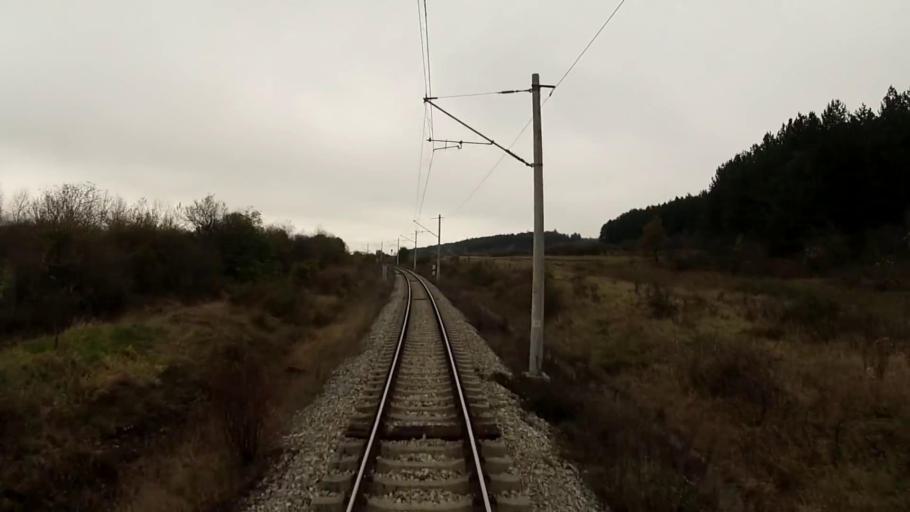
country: BG
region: Sofiya
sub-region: Obshtina Dragoman
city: Dragoman
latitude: 42.9315
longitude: 22.9139
